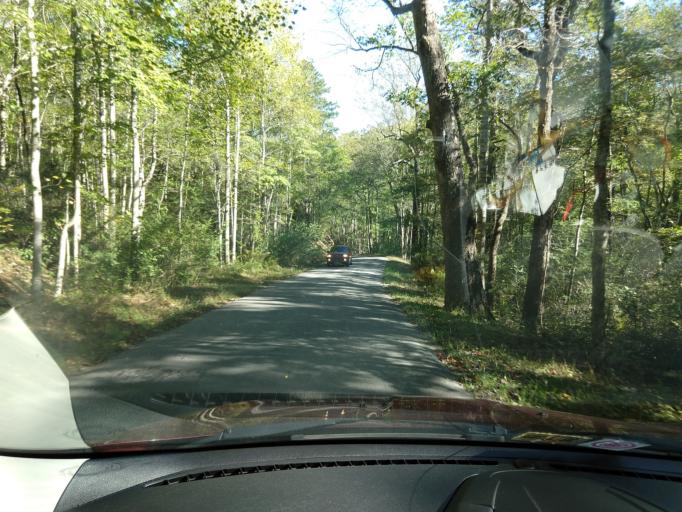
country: US
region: Virginia
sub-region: Alleghany County
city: Clifton Forge
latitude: 37.8598
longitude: -79.8777
